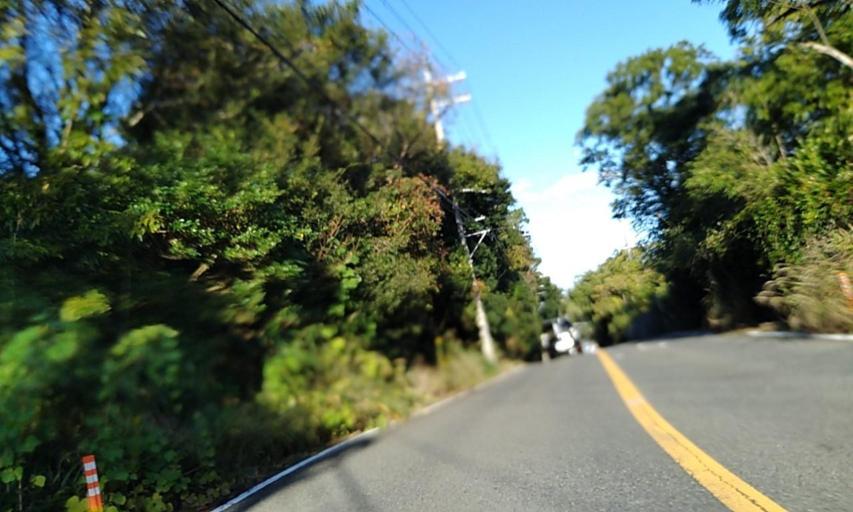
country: JP
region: Wakayama
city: Wakayama-shi
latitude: 34.3146
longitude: 135.1130
